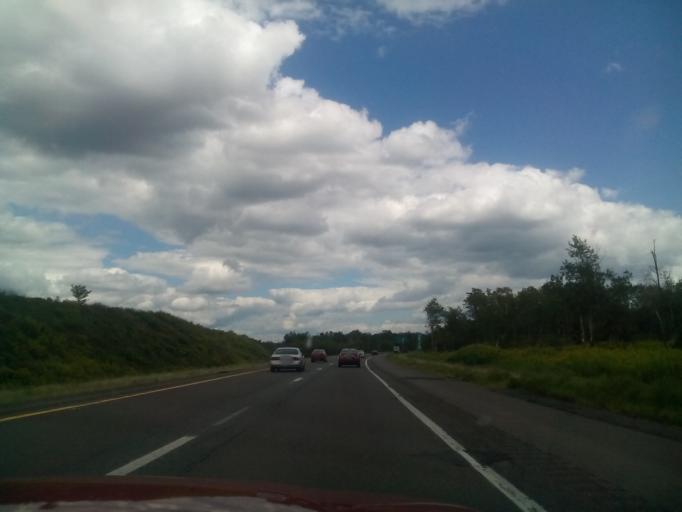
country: US
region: Pennsylvania
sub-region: Monroe County
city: Emerald Lakes
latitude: 41.0716
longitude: -75.4224
